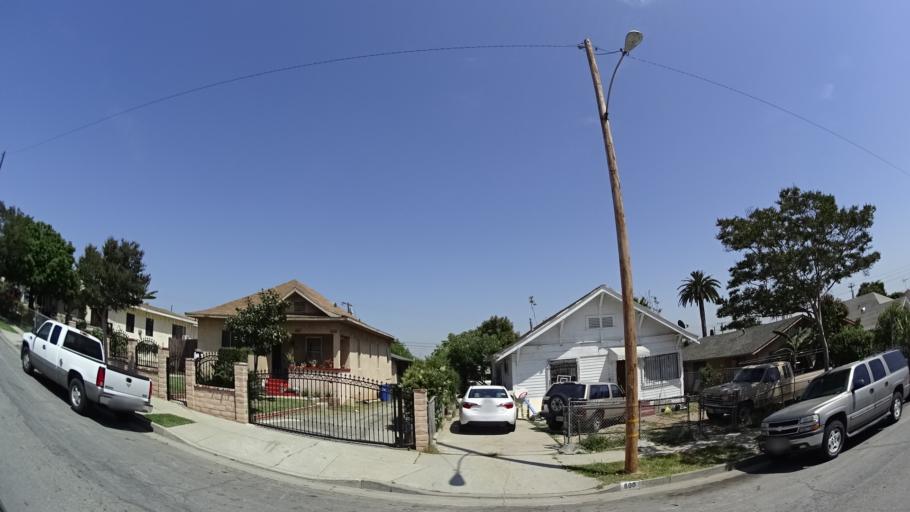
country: US
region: California
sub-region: Los Angeles County
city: Belvedere
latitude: 34.0435
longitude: -118.1811
